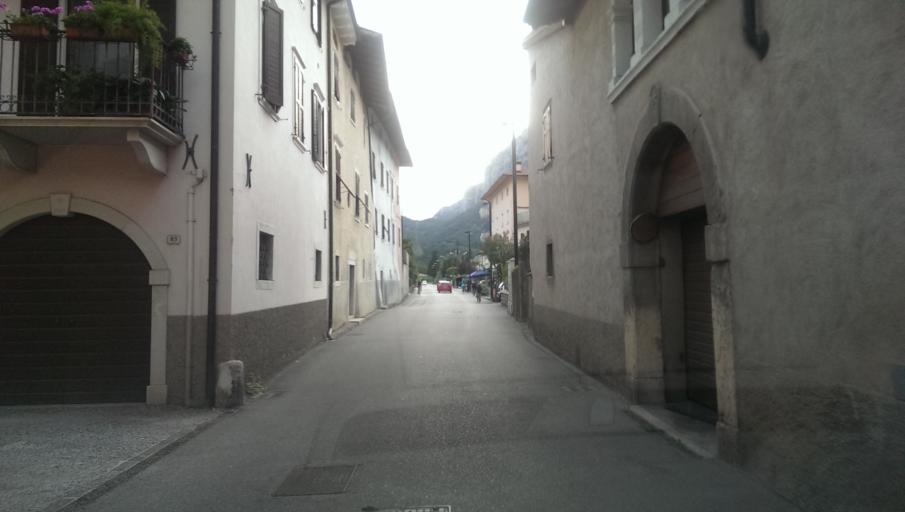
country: IT
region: Trentino-Alto Adige
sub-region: Provincia di Trento
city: Dro
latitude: 45.9595
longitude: 10.9078
